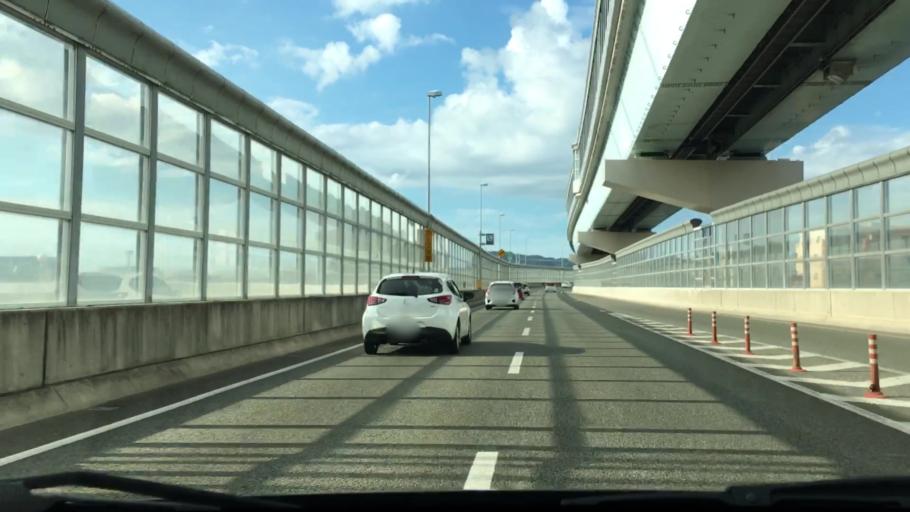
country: JP
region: Fukuoka
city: Fukuoka-shi
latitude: 33.5746
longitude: 130.3161
